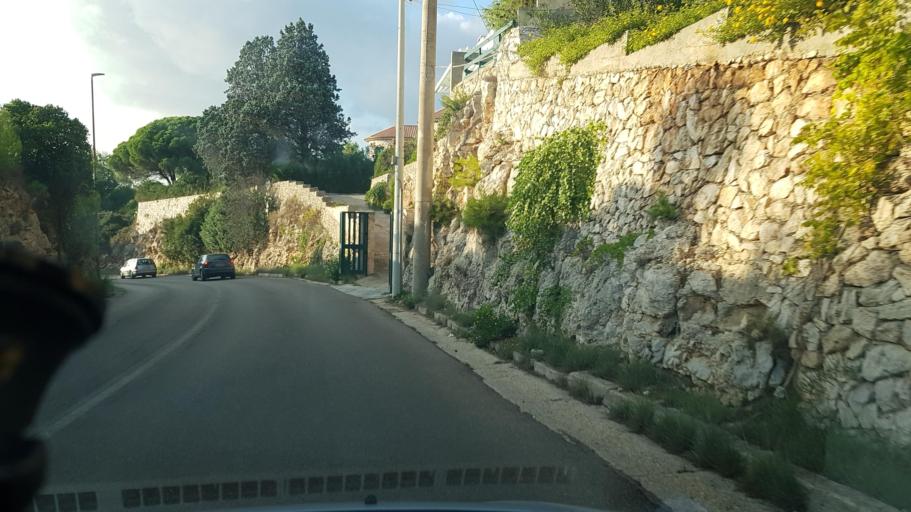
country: IT
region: Apulia
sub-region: Provincia di Lecce
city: Leuca
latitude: 39.8000
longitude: 18.3671
